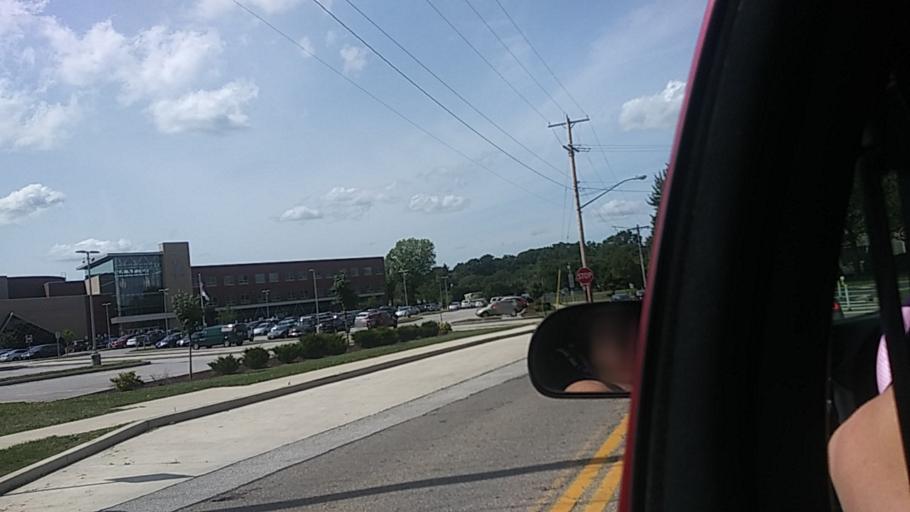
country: US
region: Ohio
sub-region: Summit County
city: Fairlawn
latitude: 41.1183
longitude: -81.5620
